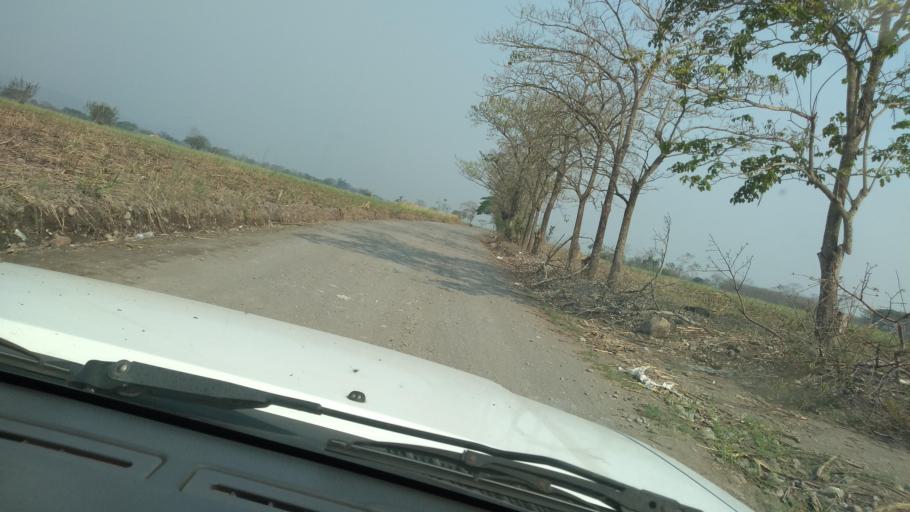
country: MX
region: Veracruz
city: Tezonapa
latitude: 18.6290
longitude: -96.6111
